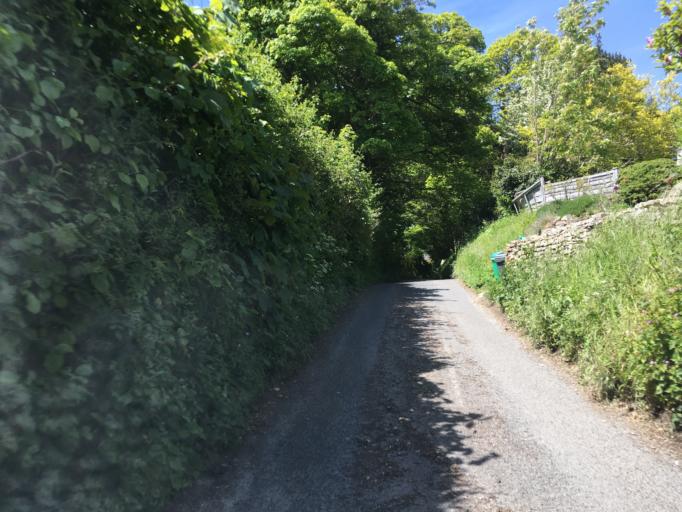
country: GB
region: England
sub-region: Gloucestershire
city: Brimscombe
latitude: 51.7212
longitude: -2.1851
